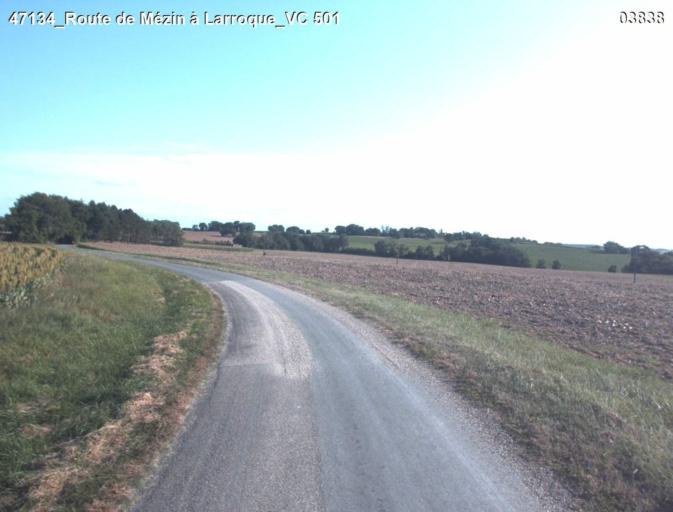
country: FR
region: Aquitaine
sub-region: Departement du Lot-et-Garonne
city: Mezin
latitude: 44.0288
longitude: 0.2676
